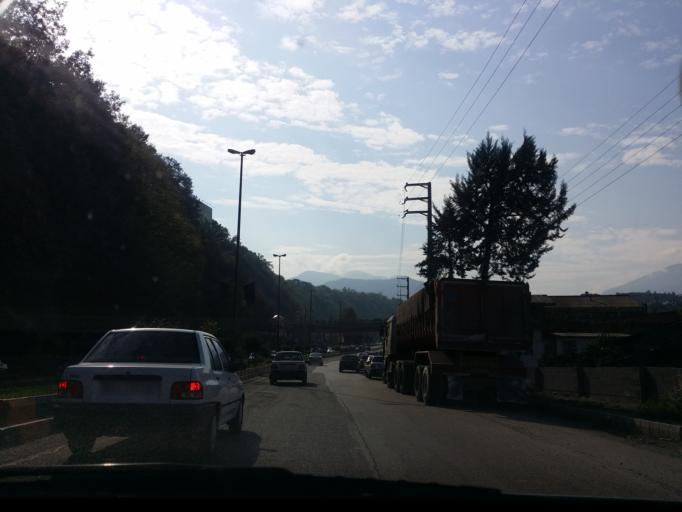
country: IR
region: Mazandaran
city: Chalus
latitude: 36.6481
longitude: 51.4139
